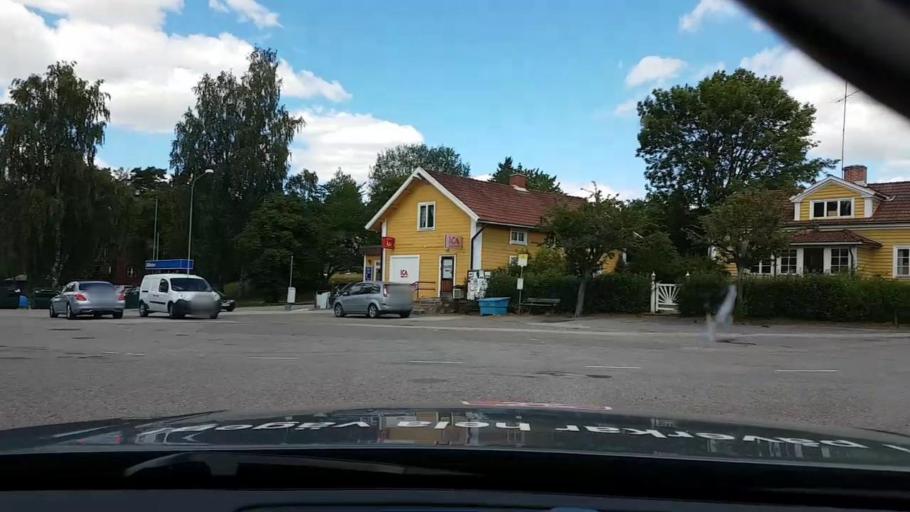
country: SE
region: Kalmar
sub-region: Vasterviks Kommun
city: Overum
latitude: 58.0799
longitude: 16.3541
